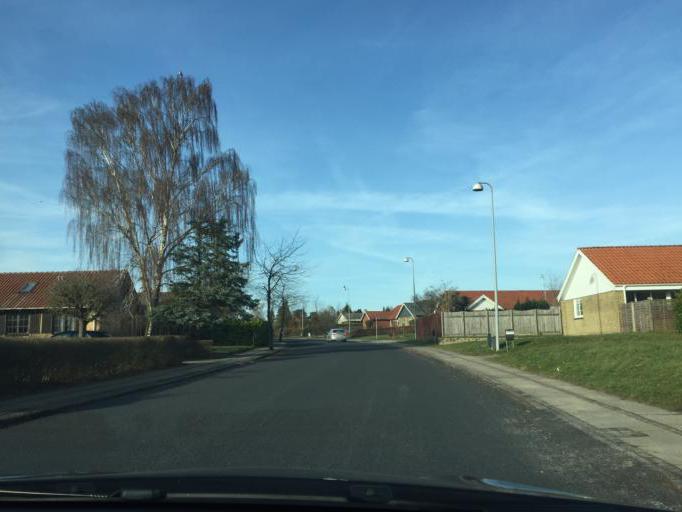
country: DK
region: South Denmark
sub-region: Odense Kommune
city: Odense
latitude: 55.3693
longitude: 10.3551
